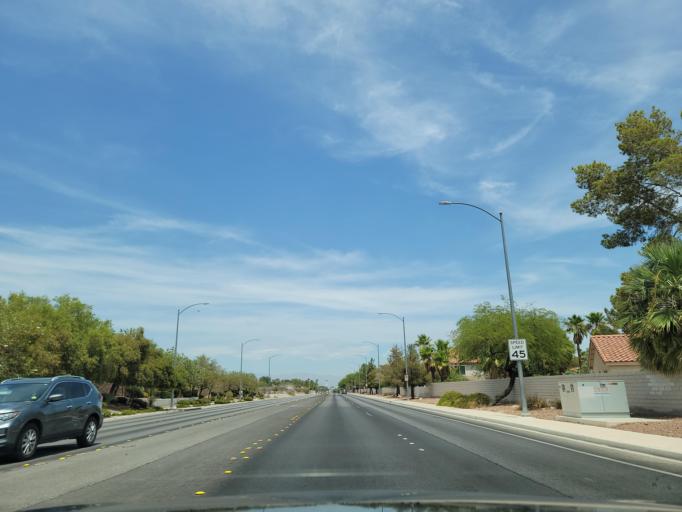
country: US
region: Nevada
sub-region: Clark County
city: Paradise
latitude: 36.0356
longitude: -115.1544
